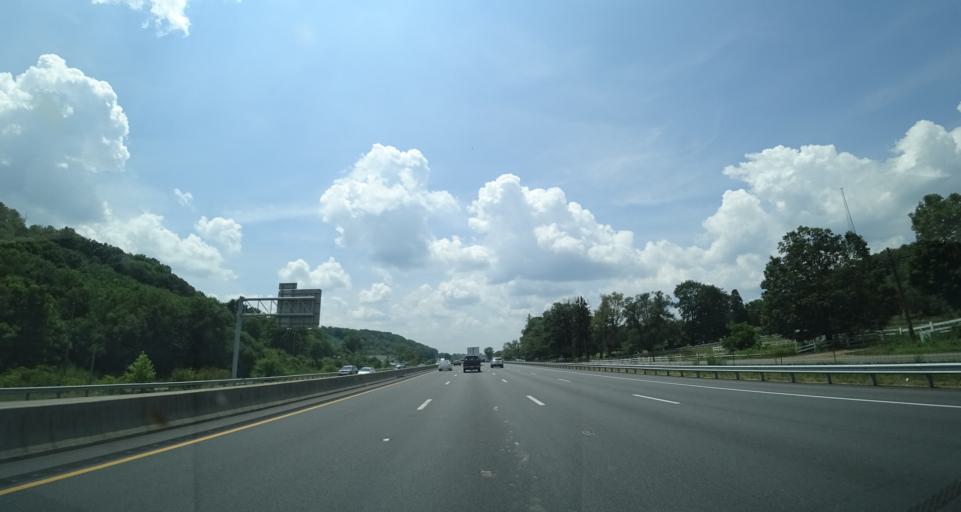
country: US
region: Virginia
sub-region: Wythe County
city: Wytheville
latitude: 36.9458
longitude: -80.9531
